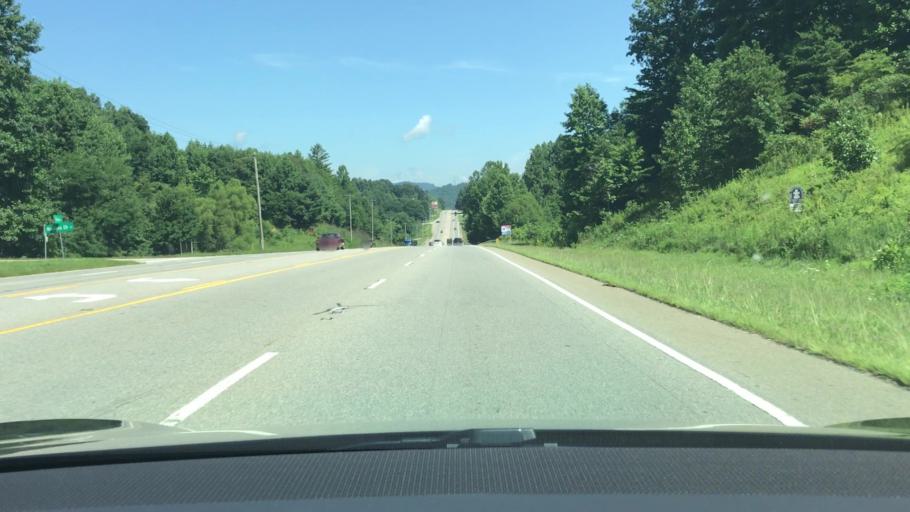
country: US
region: North Carolina
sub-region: Macon County
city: Franklin
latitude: 35.1069
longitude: -83.3871
